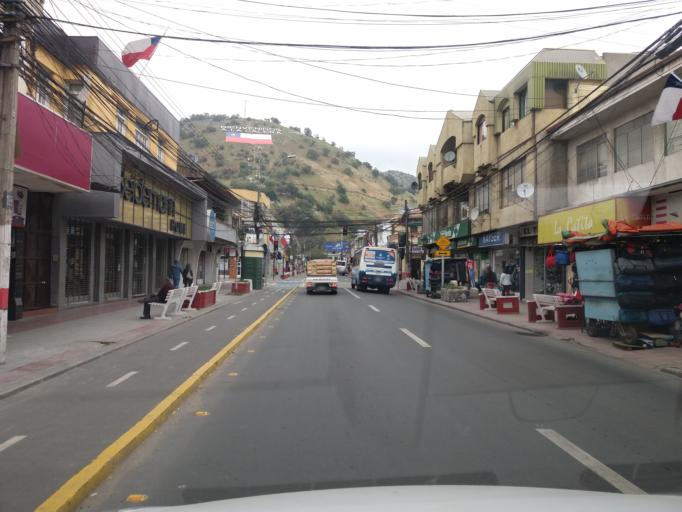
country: CL
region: Valparaiso
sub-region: Provincia de Quillota
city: Hacienda La Calera
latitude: -32.7877
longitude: -71.1896
